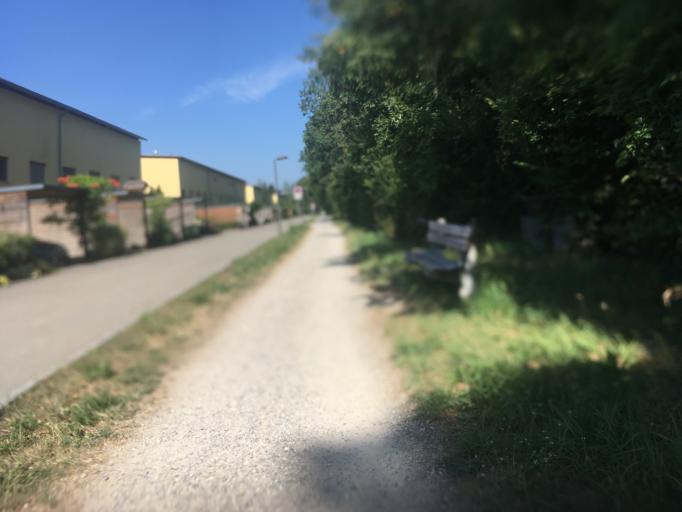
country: CH
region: Bern
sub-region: Emmental District
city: Burgdorf
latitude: 47.0677
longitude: 7.6116
